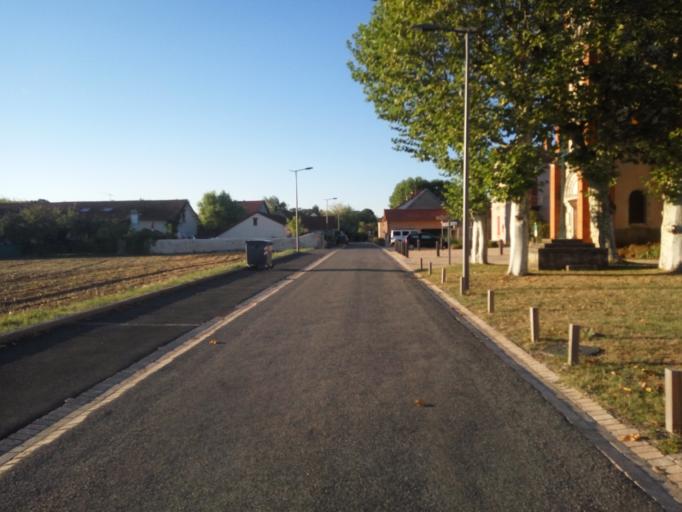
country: FR
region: Auvergne
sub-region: Departement de l'Allier
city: Brugheas
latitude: 46.0972
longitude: 3.3585
